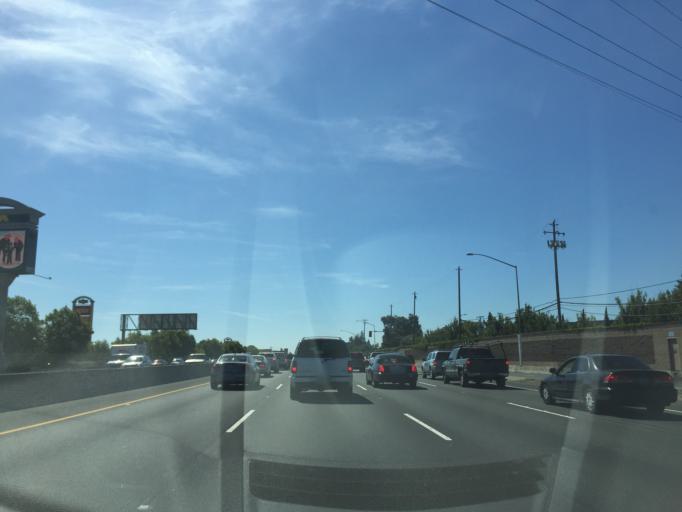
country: US
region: California
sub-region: San Mateo County
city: East Palo Alto
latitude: 37.4594
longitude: -122.1393
